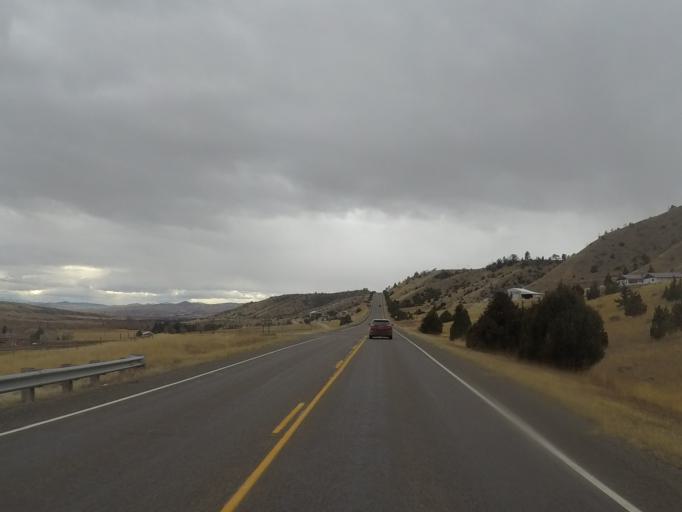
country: US
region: Montana
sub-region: Broadwater County
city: Townsend
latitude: 46.3256
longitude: -111.4022
